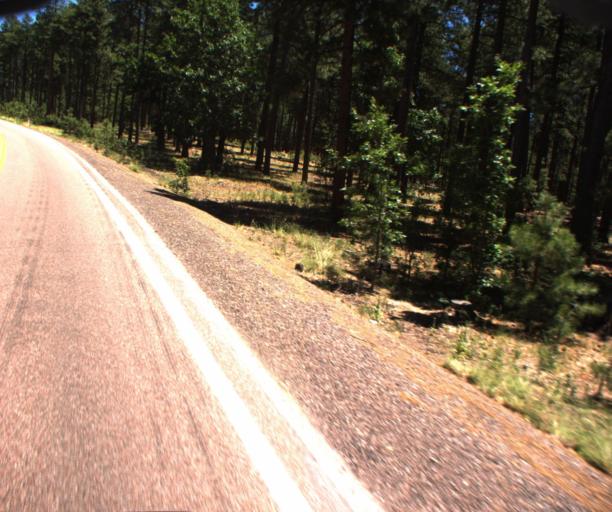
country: US
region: Arizona
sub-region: Gila County
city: Pine
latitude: 34.4415
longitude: -111.4680
